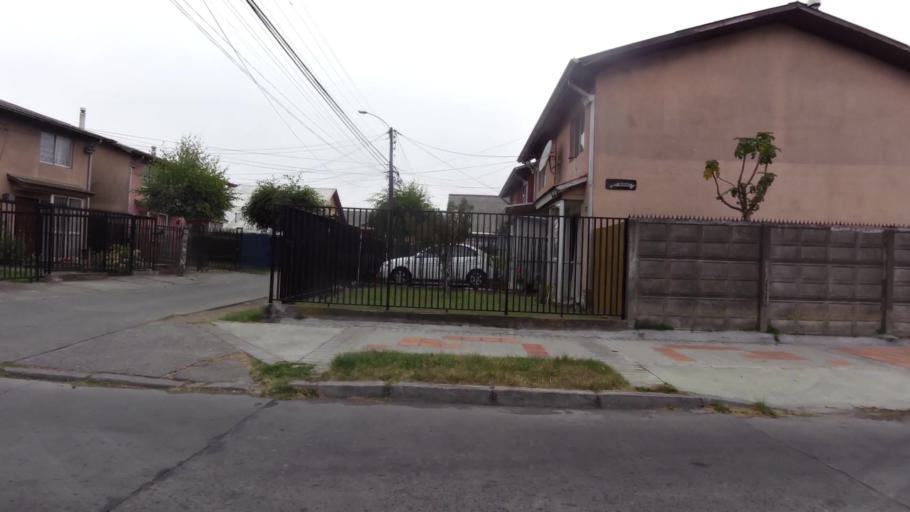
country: CL
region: Biobio
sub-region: Provincia de Concepcion
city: Concepcion
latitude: -36.7919
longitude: -73.0824
